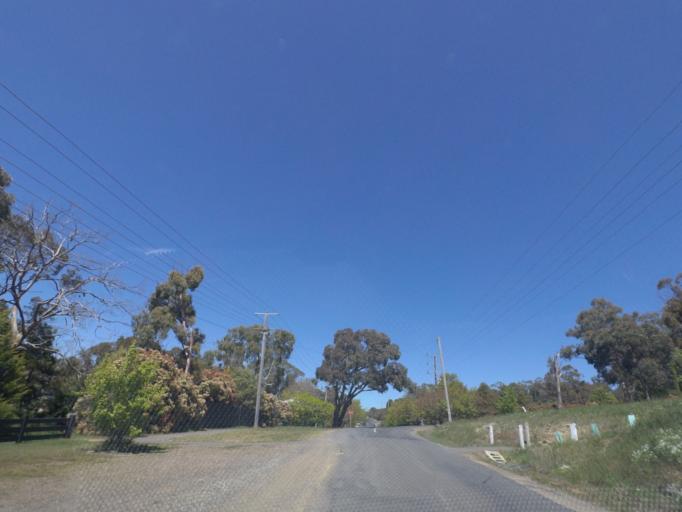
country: AU
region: Victoria
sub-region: Hume
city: Sunbury
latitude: -37.4166
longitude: 144.5620
